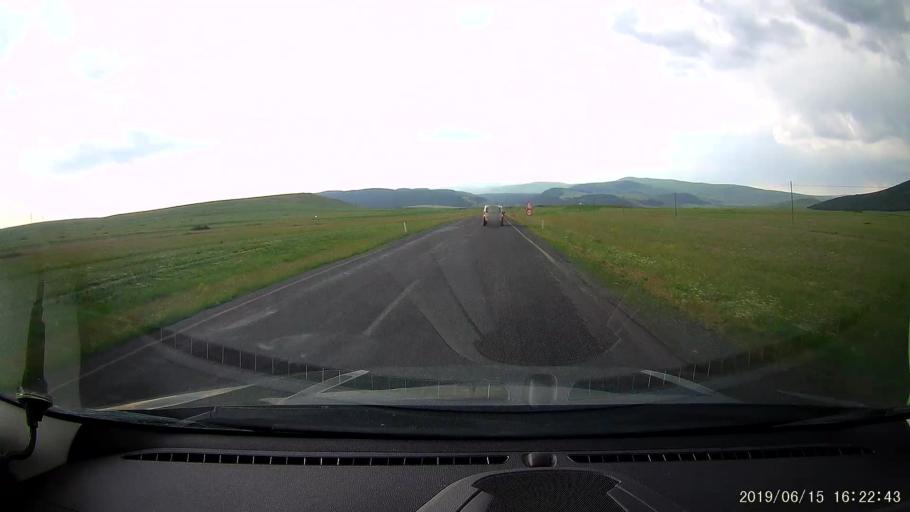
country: TR
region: Ardahan
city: Hanak
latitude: 41.1854
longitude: 42.8537
